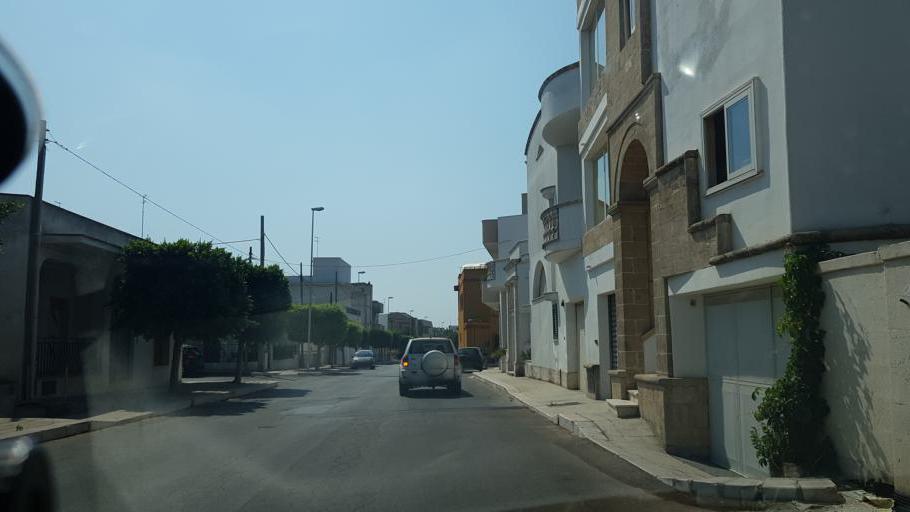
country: IT
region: Apulia
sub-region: Provincia di Taranto
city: Maruggio
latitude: 40.3257
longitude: 17.5732
